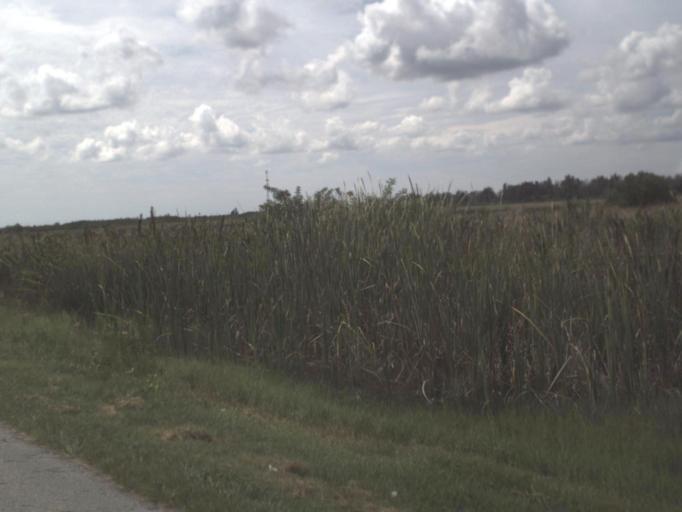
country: US
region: Florida
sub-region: Collier County
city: Marco
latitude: 25.9202
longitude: -81.3587
